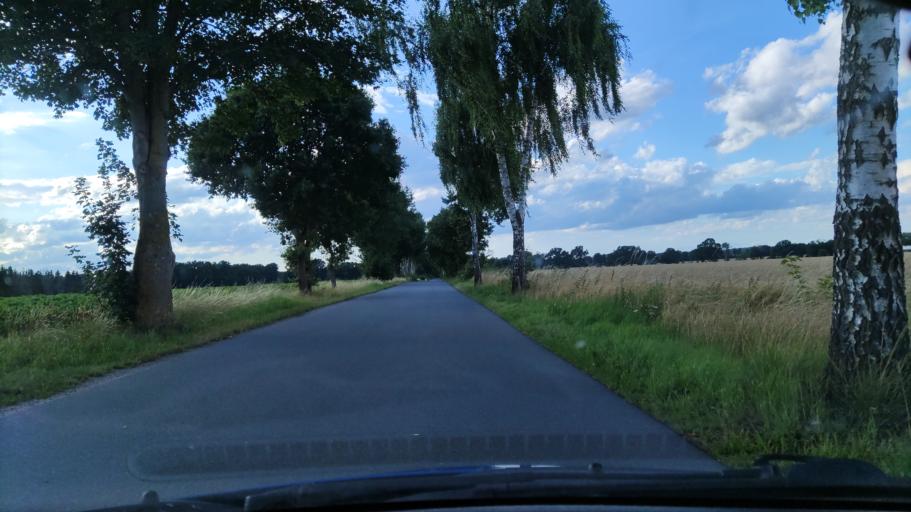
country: DE
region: Lower Saxony
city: Dahlenburg
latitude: 53.1722
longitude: 10.7028
